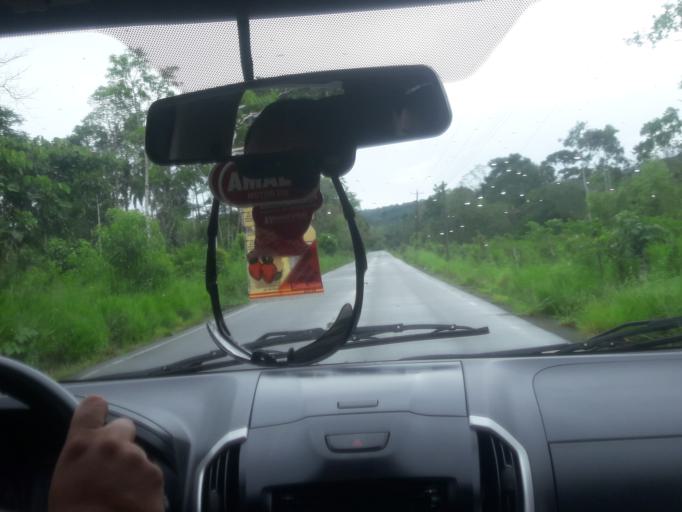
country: EC
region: Napo
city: Tena
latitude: -1.0343
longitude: -77.6817
